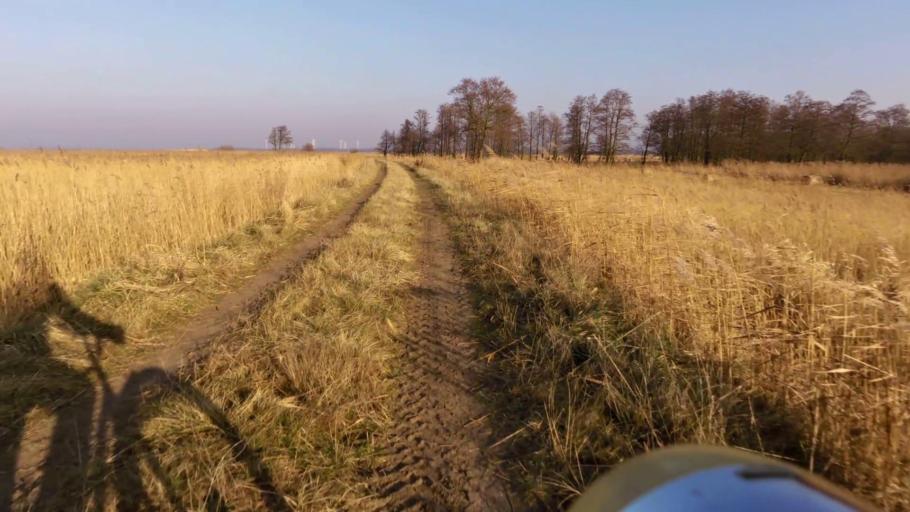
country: PL
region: West Pomeranian Voivodeship
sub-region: Powiat kamienski
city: Wolin
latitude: 53.7595
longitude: 14.5898
